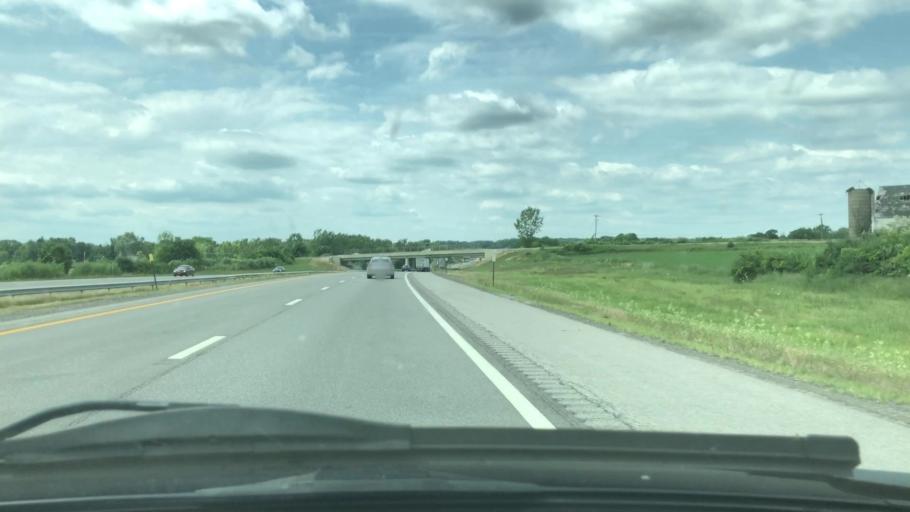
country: US
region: New York
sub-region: Genesee County
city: Batavia
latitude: 43.0146
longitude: -78.1084
